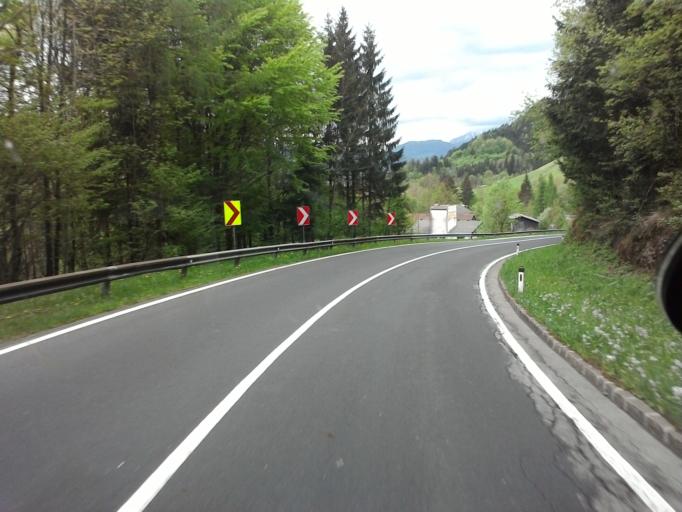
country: AT
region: Upper Austria
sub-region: Politischer Bezirk Kirchdorf an der Krems
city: Rossleithen
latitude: 47.7452
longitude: 14.2505
